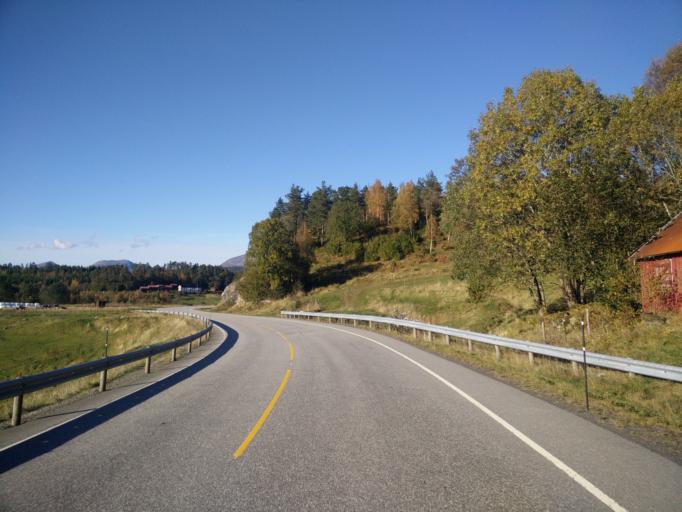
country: NO
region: More og Romsdal
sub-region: Halsa
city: Liaboen
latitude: 63.0971
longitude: 8.3451
